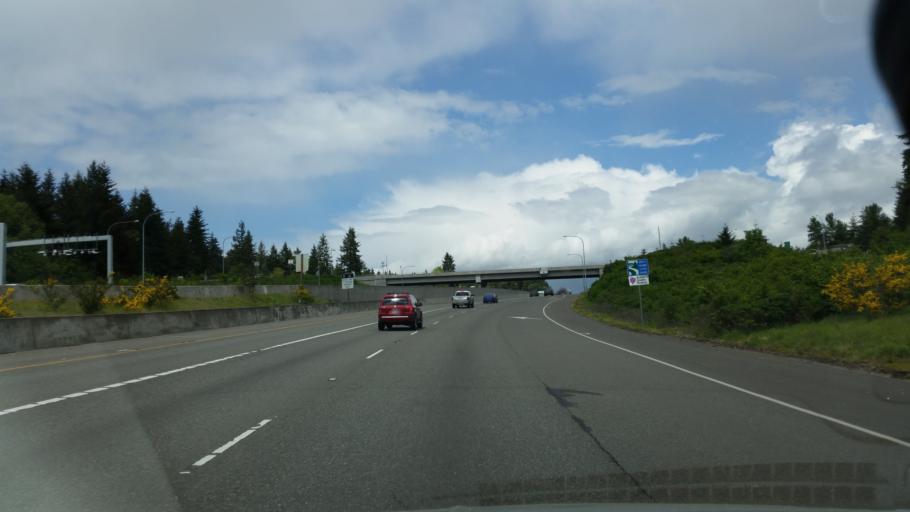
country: US
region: Washington
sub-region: Pierce County
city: Wollochet
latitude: 47.2773
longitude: -122.5603
